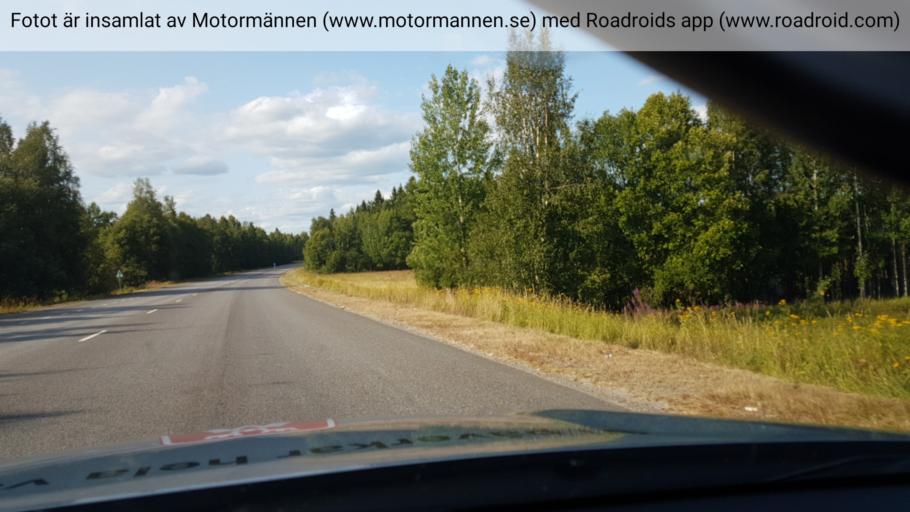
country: SE
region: Norrbotten
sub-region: Pitea Kommun
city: Pitea
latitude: 65.2794
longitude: 21.5121
